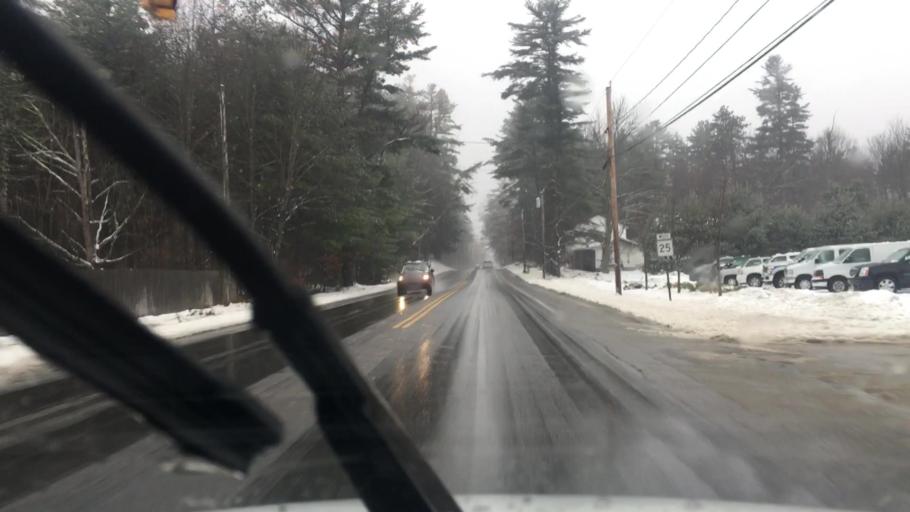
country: US
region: Maine
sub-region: York County
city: Buxton
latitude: 43.7190
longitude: -70.5249
